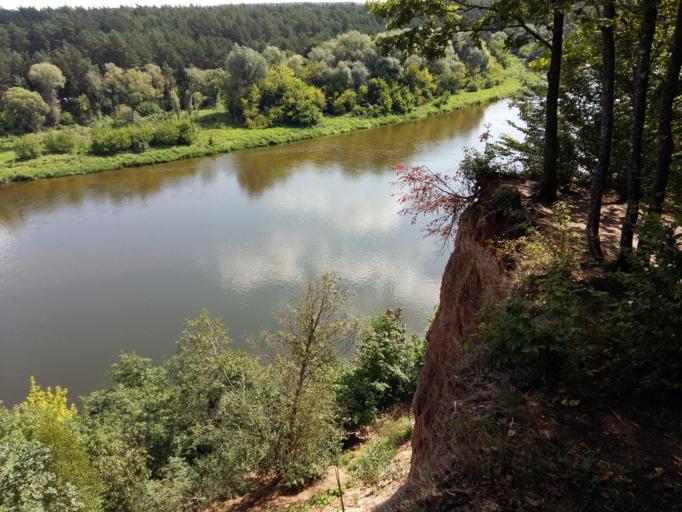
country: LT
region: Kauno apskritis
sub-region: Kauno rajonas
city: Karmelava
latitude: 55.0184
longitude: 24.1077
